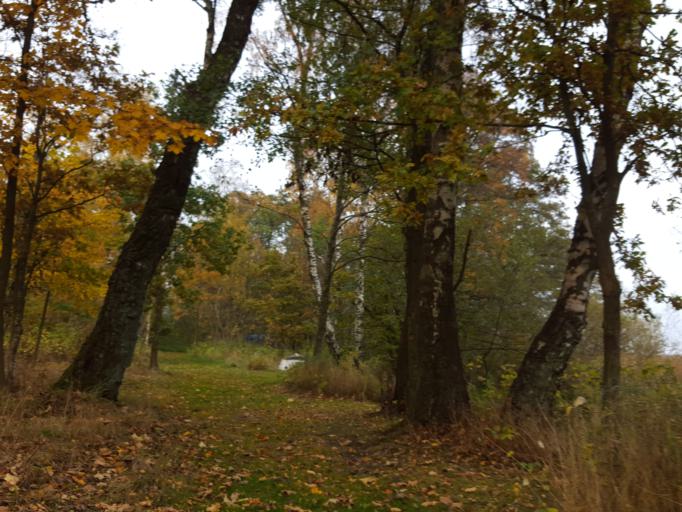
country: SE
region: Skane
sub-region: Eslovs Kommun
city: Stehag
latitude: 55.9043
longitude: 13.4371
